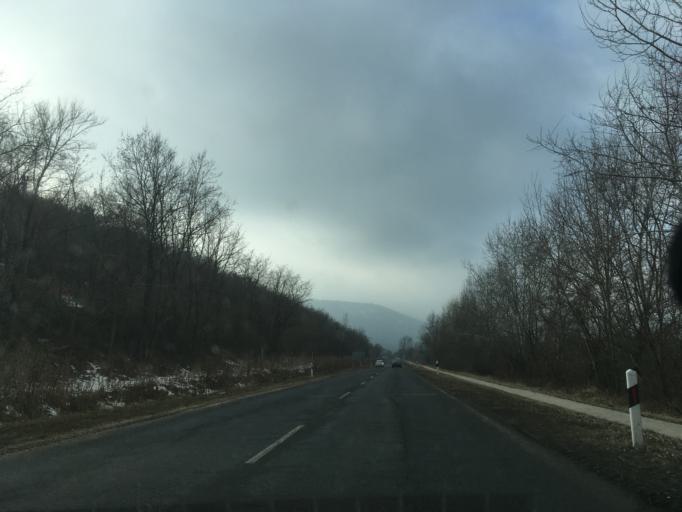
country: HU
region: Pest
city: Visegrad
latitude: 47.7693
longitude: 18.9593
